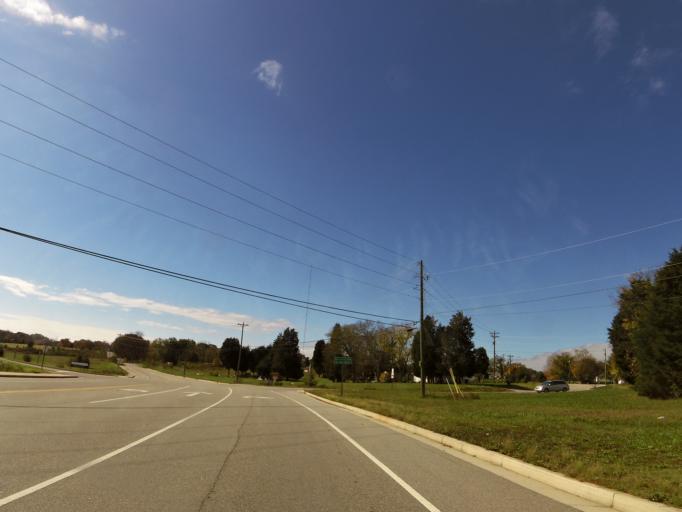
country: US
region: Tennessee
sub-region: Blount County
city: Maryville
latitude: 35.7681
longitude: -84.0129
